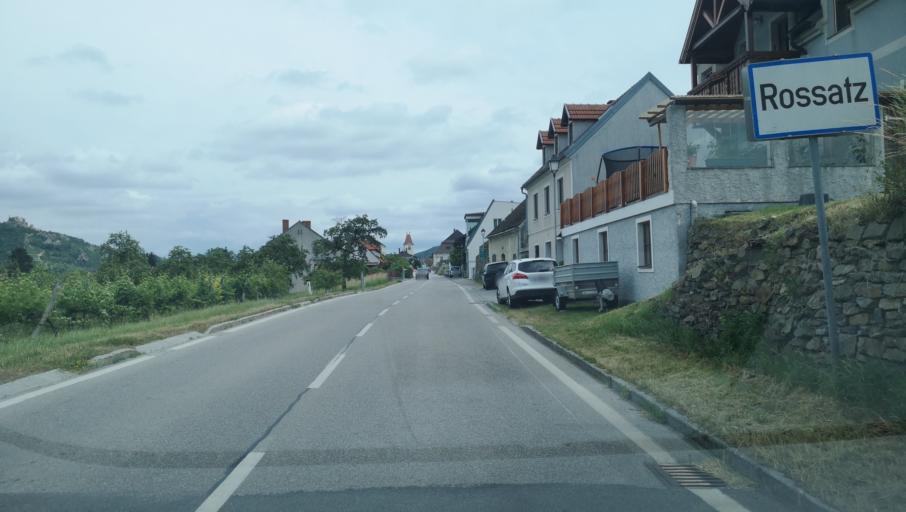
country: AT
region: Lower Austria
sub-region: Politischer Bezirk Krems
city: Durnstein
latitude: 48.3984
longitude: 15.4996
